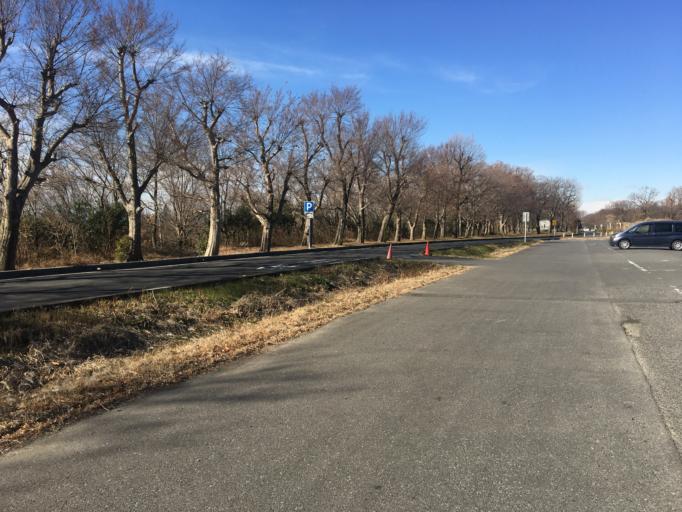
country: JP
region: Saitama
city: Shiki
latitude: 35.8515
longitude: 139.5988
